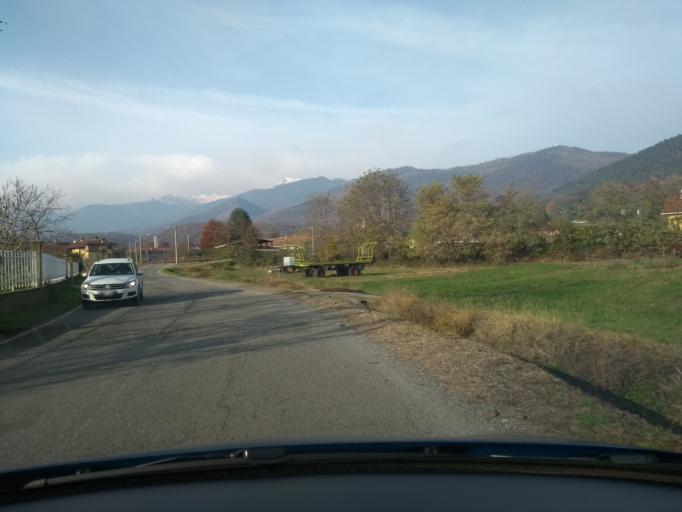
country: IT
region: Piedmont
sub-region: Provincia di Torino
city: Balangero
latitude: 45.2691
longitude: 7.5244
